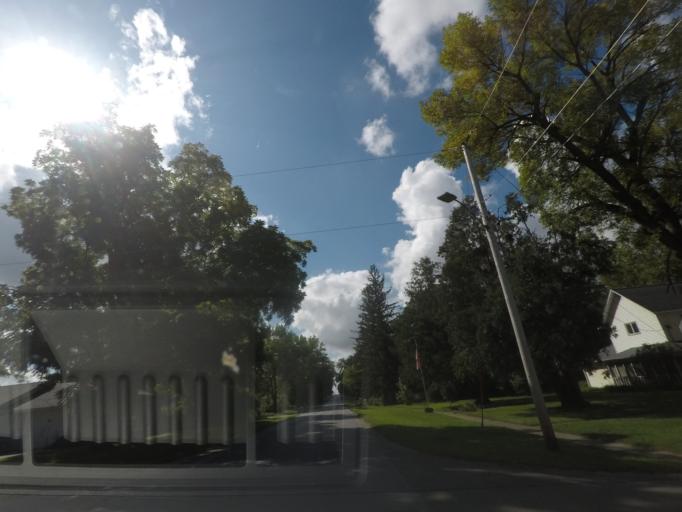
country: US
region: Iowa
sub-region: Story County
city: Nevada
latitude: 42.0165
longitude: -93.3192
